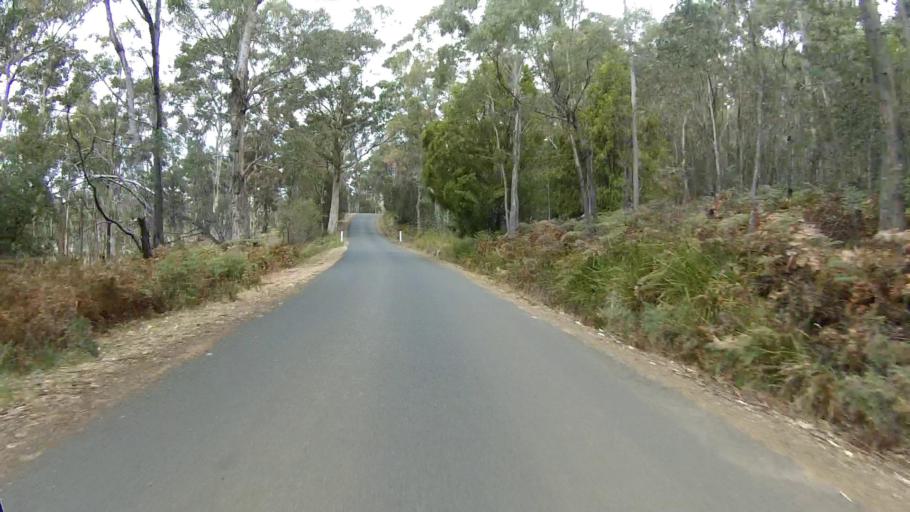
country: AU
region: Tasmania
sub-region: Sorell
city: Sorell
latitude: -42.6051
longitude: 147.9221
